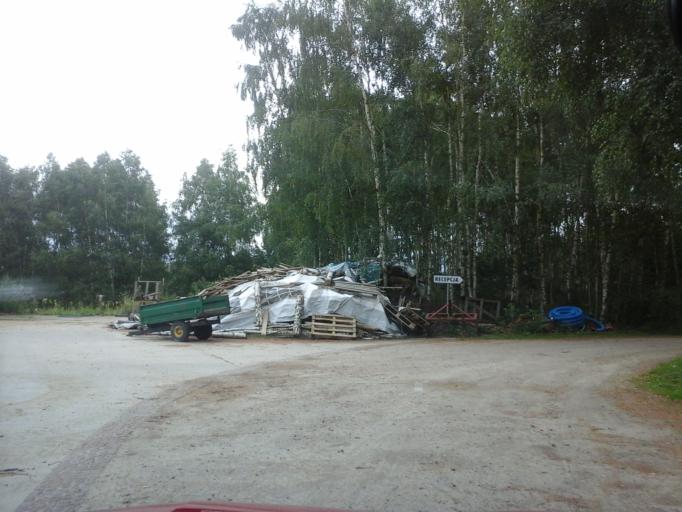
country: PL
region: West Pomeranian Voivodeship
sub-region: Powiat choszczenski
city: Krzecin
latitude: 53.1408
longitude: 15.4792
